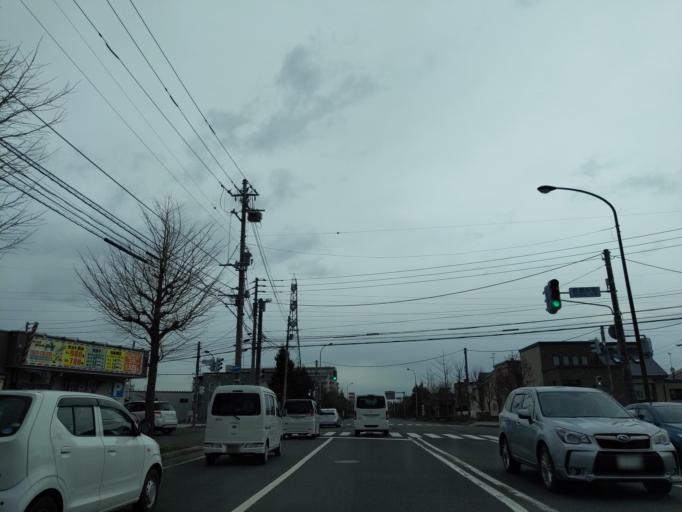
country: JP
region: Hokkaido
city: Sapporo
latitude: 43.1383
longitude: 141.3692
